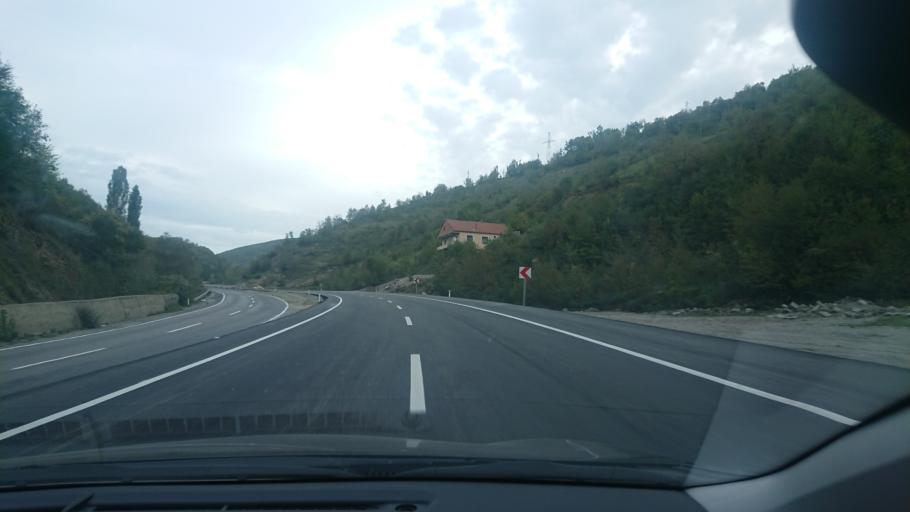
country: TR
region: Zonguldak
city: Beycuma
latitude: 41.3931
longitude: 31.9365
